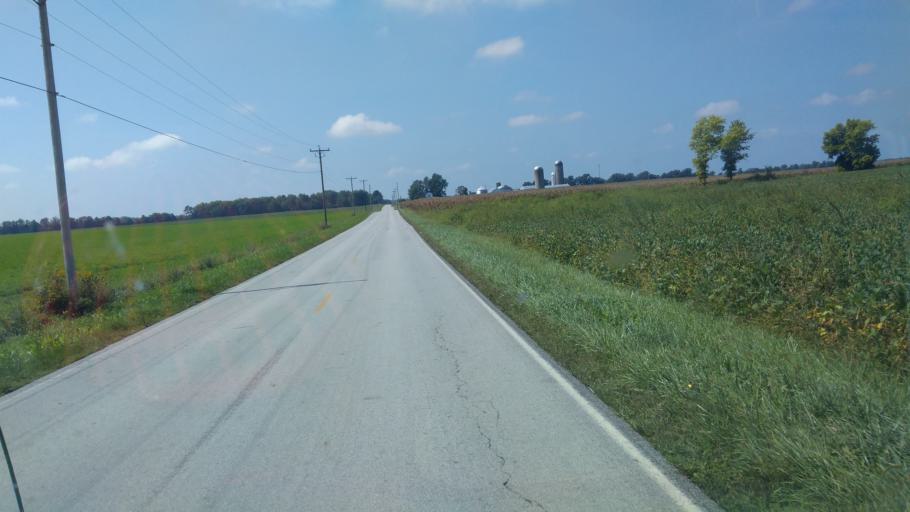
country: US
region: Ohio
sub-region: Hardin County
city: Kenton
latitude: 40.6663
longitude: -83.5793
